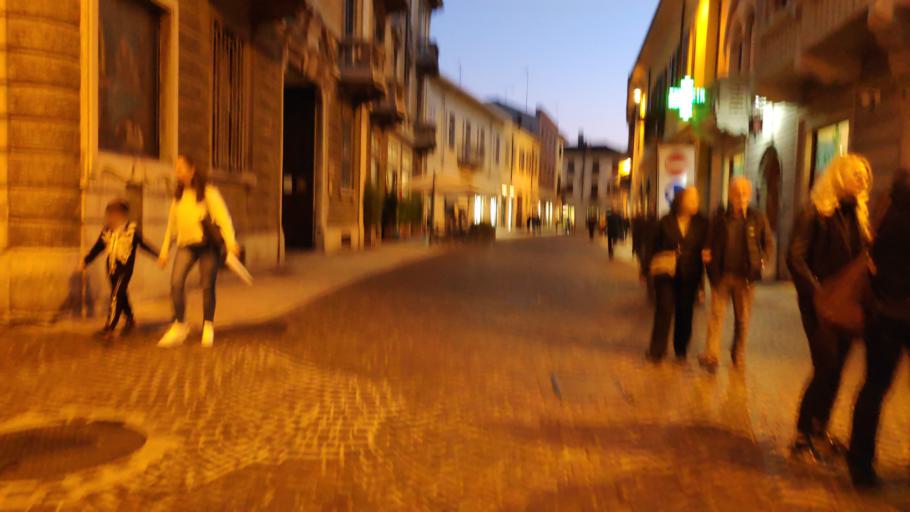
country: IT
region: Lombardy
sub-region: Citta metropolitana di Milano
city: Abbiategrasso
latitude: 45.3999
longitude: 8.9167
